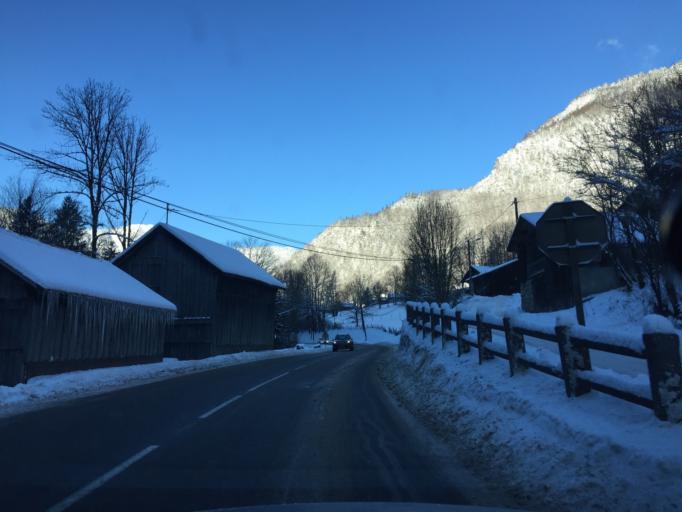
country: FR
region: Rhone-Alpes
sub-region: Departement de la Haute-Savoie
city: Abondance
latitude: 46.2828
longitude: 6.7044
